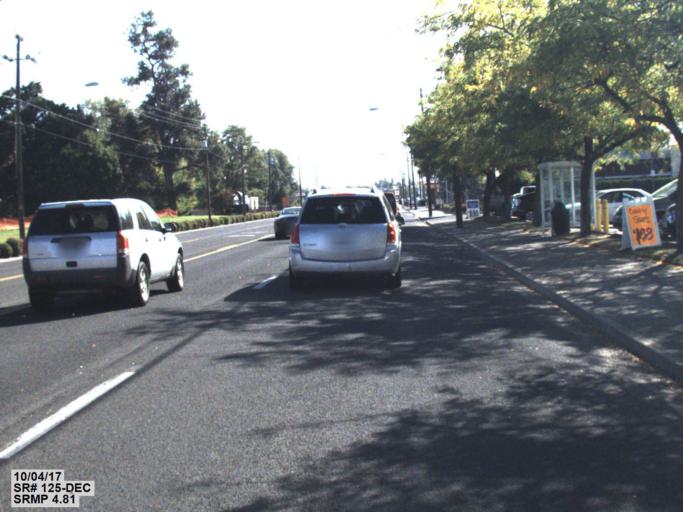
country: US
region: Washington
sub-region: Walla Walla County
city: Walla Walla
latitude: 46.0558
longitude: -118.3461
